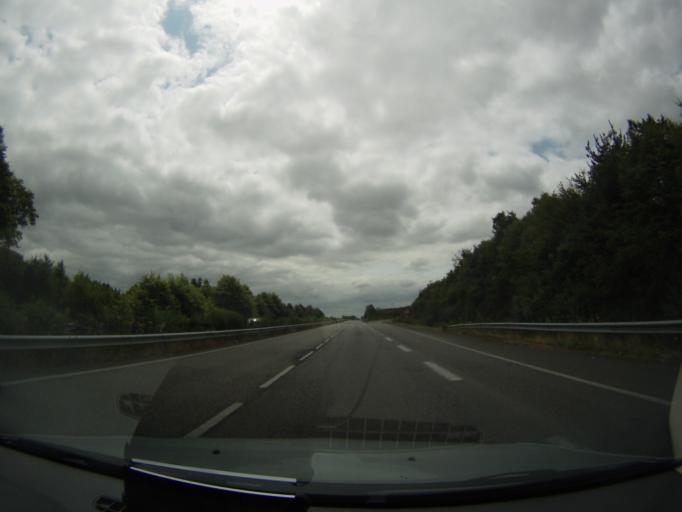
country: FR
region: Pays de la Loire
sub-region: Departement de la Loire-Atlantique
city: Nozay
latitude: 47.5384
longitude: -1.6365
